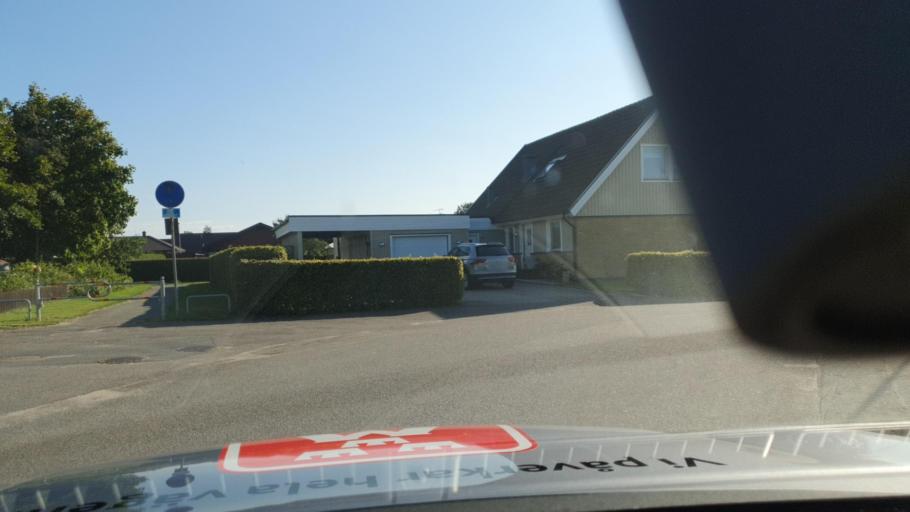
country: SE
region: Skane
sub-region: Bromolla Kommun
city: Bromoella
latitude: 56.0846
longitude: 14.4849
